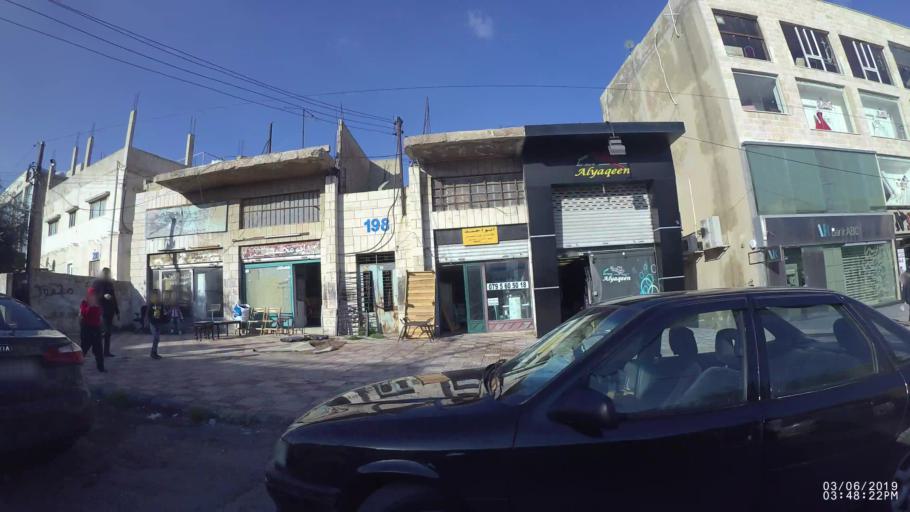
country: JO
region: Amman
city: Amman
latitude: 31.9718
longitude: 35.9516
